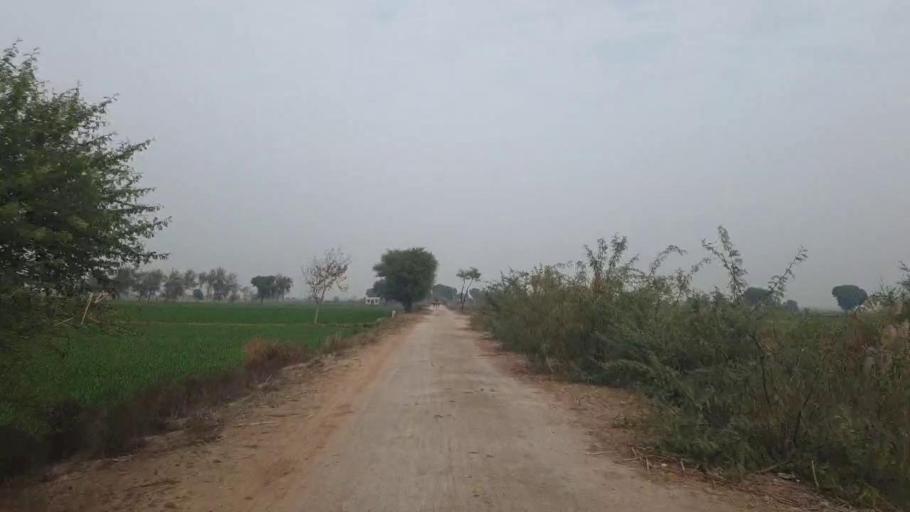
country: PK
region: Sindh
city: Tando Adam
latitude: 25.7265
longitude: 68.7386
